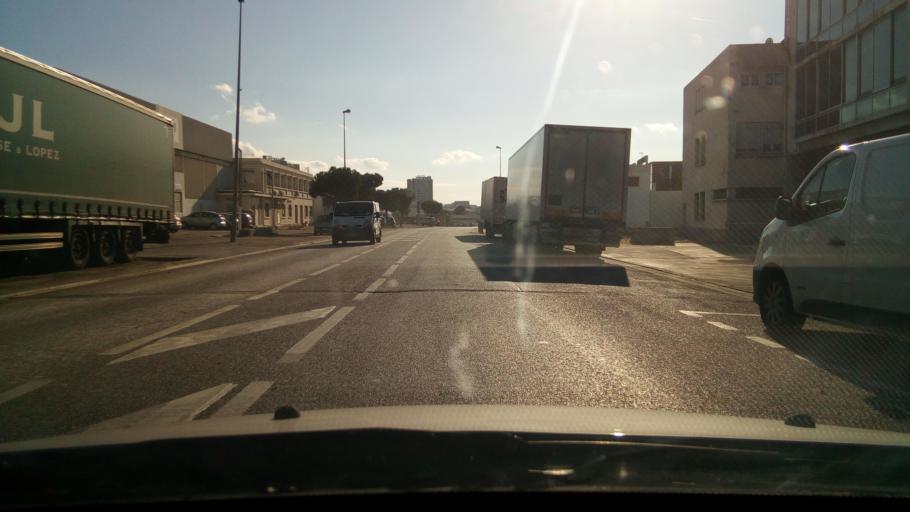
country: FR
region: Provence-Alpes-Cote d'Azur
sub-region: Departement des Bouches-du-Rhone
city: Marseille 14
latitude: 43.3379
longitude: 5.3736
